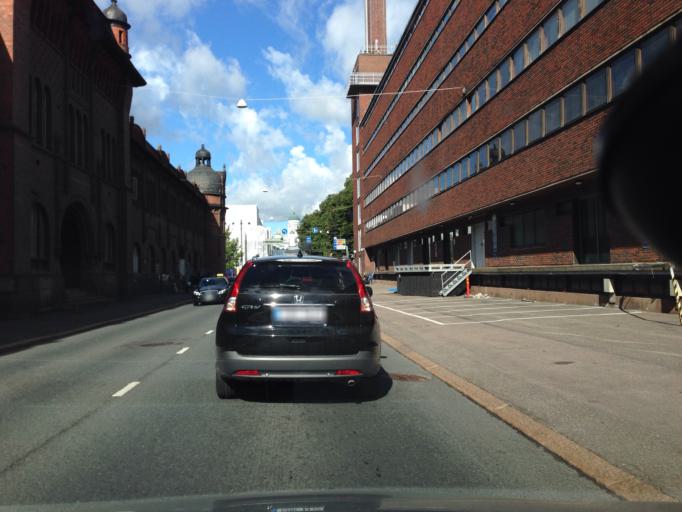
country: FI
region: Uusimaa
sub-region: Helsinki
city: Helsinki
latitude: 60.1667
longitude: 24.9630
